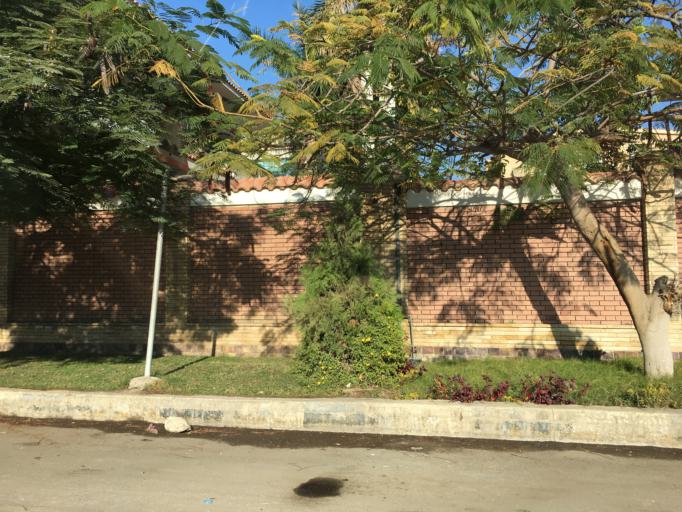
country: EG
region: Al Jizah
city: Madinat Sittah Uktubar
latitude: 29.9859
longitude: 30.9433
